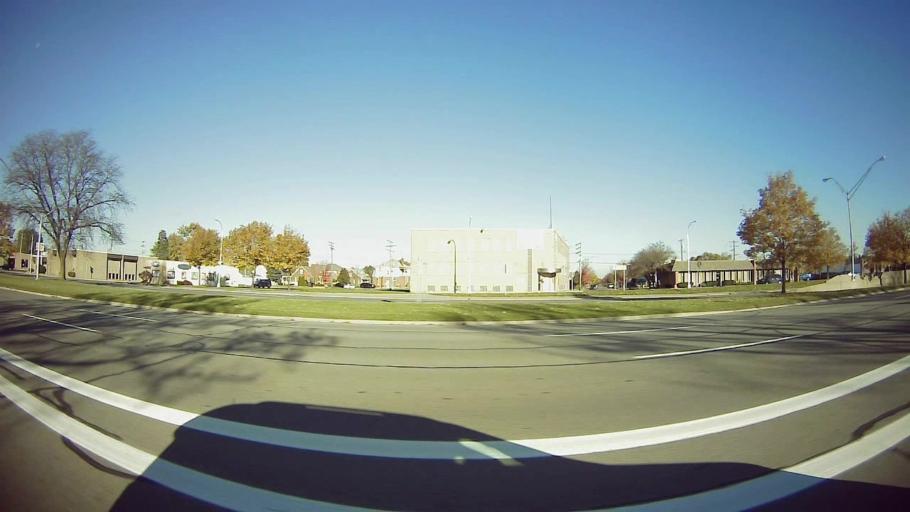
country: US
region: Michigan
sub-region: Wayne County
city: Dearborn
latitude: 42.3158
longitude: -83.1972
